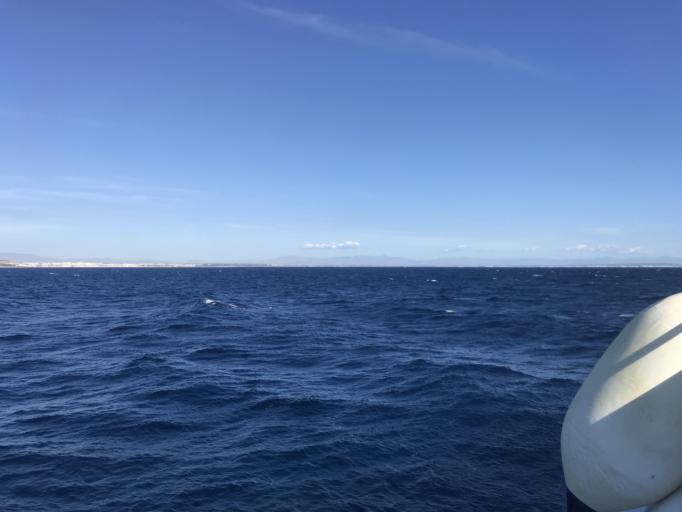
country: ES
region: Valencia
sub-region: Provincia de Alicante
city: Guardamar del Segura
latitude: 38.0335
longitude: -0.6127
